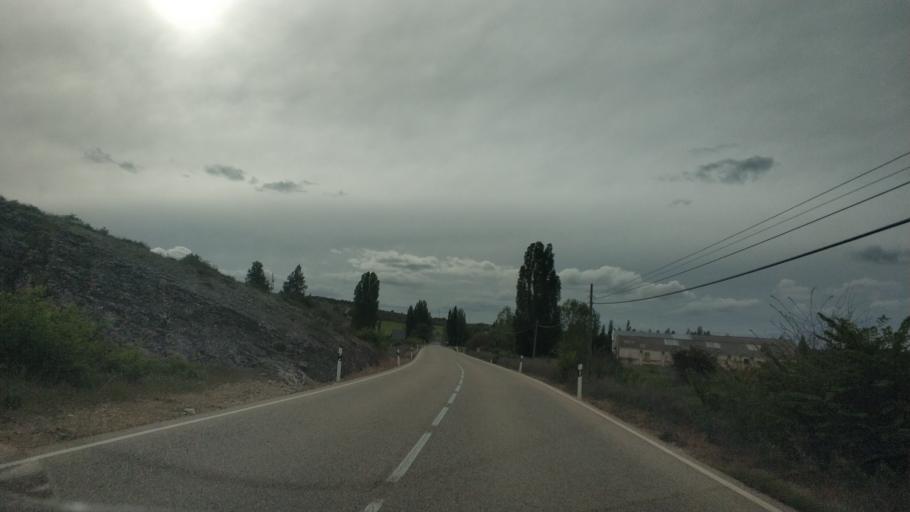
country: ES
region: Castille and Leon
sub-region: Provincia de Soria
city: El Burgo de Osma
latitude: 41.5789
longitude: -3.0342
